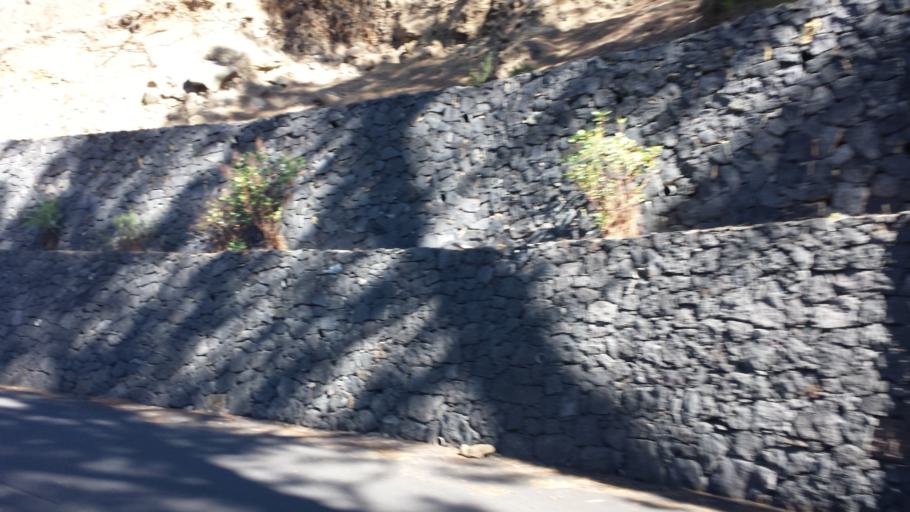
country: ES
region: Canary Islands
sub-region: Provincia de Santa Cruz de Tenerife
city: El Paso
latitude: 28.6970
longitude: -17.8519
